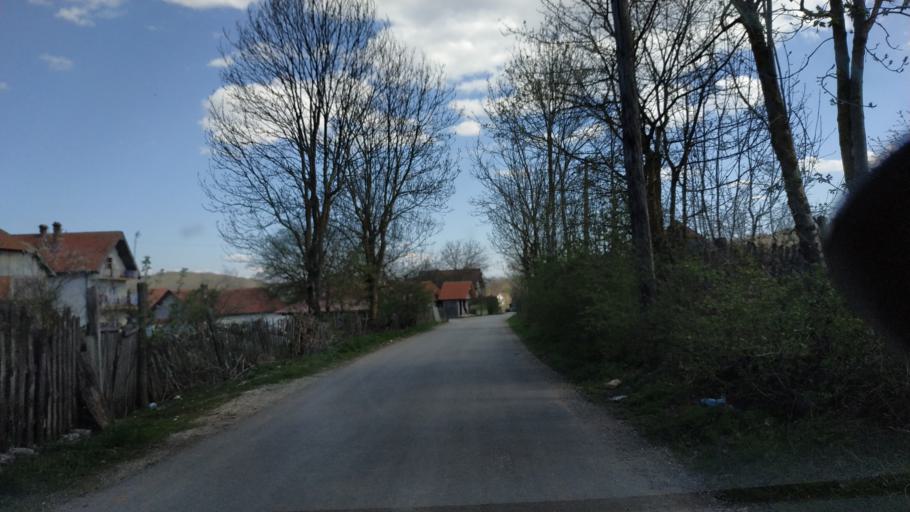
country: RS
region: Central Serbia
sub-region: Zajecarski Okrug
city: Soko Banja
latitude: 43.5718
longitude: 21.9003
